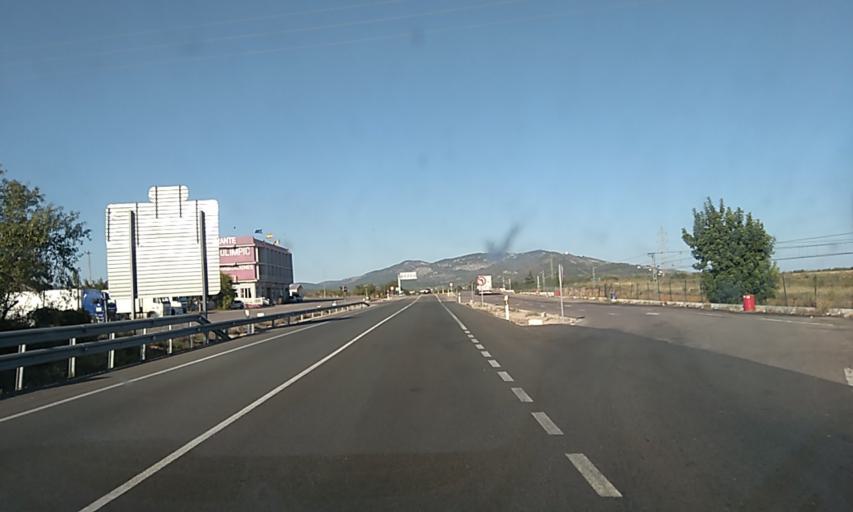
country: ES
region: Valencia
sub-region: Provincia de Castello
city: Torreblanca
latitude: 40.2320
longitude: 0.2193
